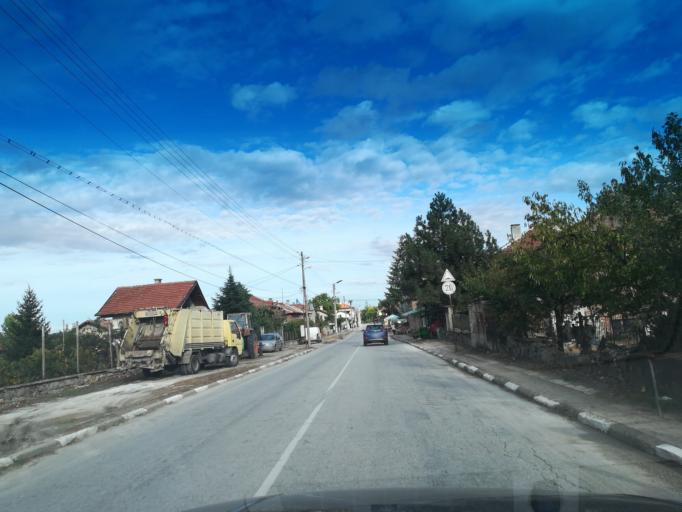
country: BG
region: Pazardzhik
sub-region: Obshtina Bratsigovo
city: Bratsigovo
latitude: 42.0649
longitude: 24.3720
